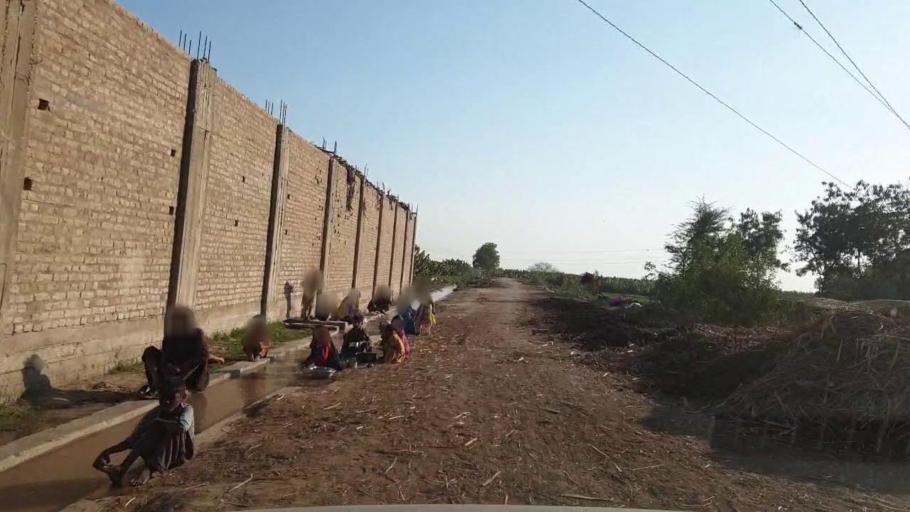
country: PK
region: Sindh
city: Tando Allahyar
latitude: 25.3464
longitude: 68.6818
